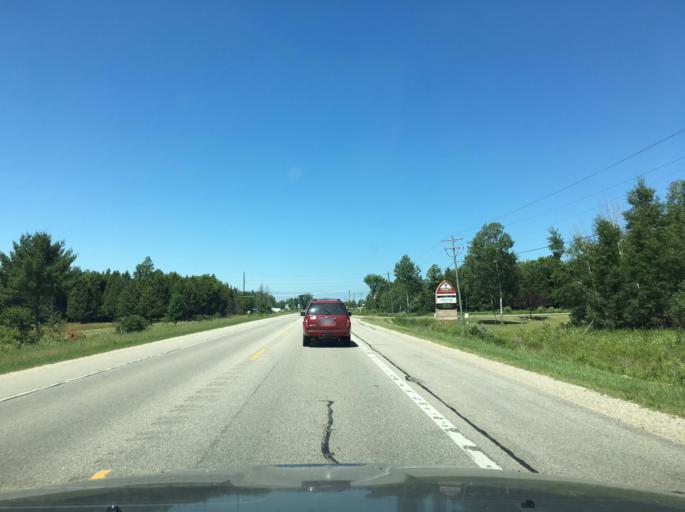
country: US
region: Michigan
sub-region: Osceola County
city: Reed City
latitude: 43.8730
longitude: -85.4790
